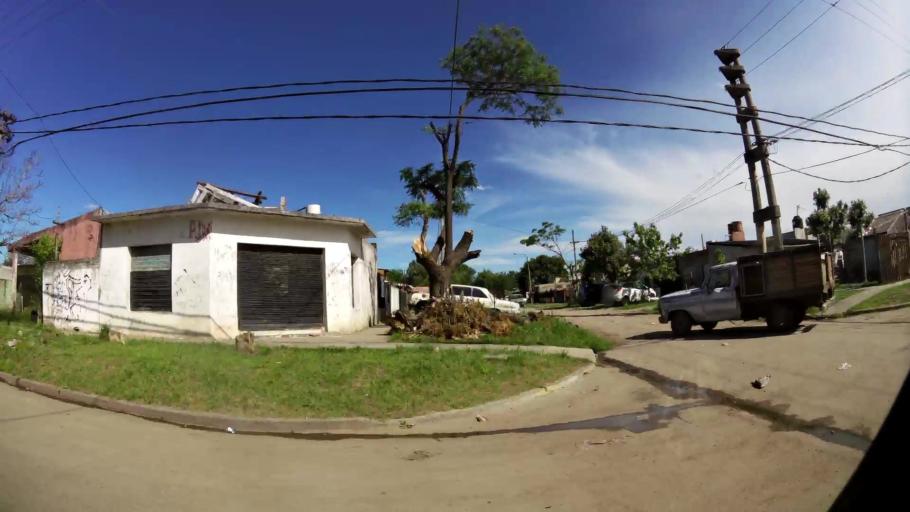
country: AR
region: Buenos Aires
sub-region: Partido de Almirante Brown
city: Adrogue
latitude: -34.8021
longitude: -58.3590
